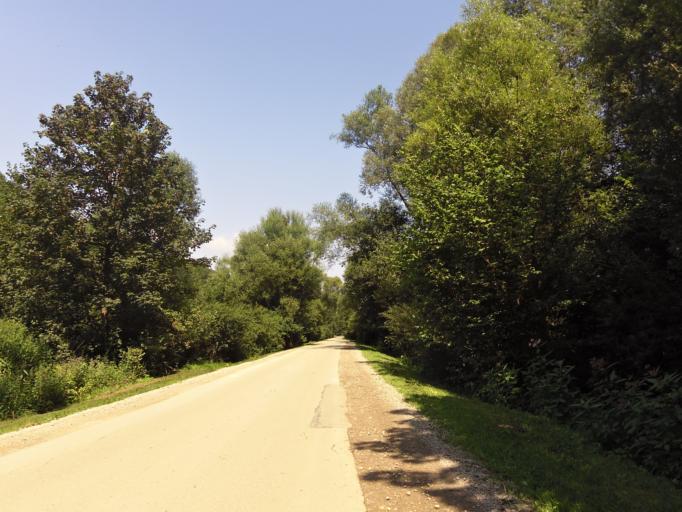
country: PL
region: Silesian Voivodeship
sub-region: Powiat zywiecki
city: Cisiec
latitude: 49.5966
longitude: 19.0998
